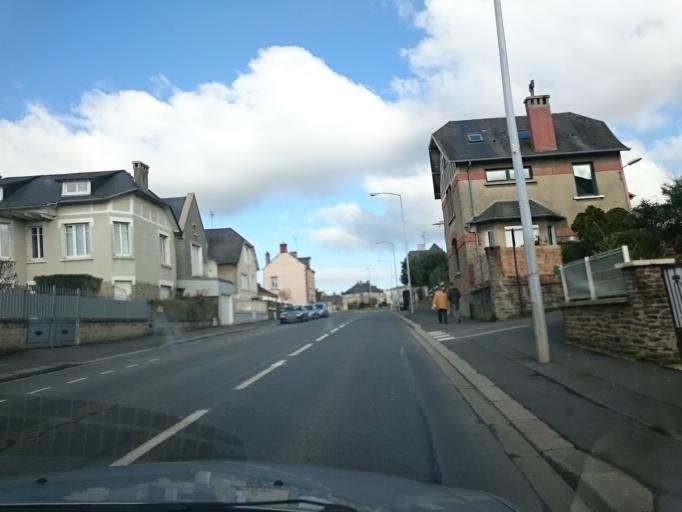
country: FR
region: Lower Normandy
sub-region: Departement de la Manche
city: Saint-Lo
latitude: 49.1145
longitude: -1.0813
